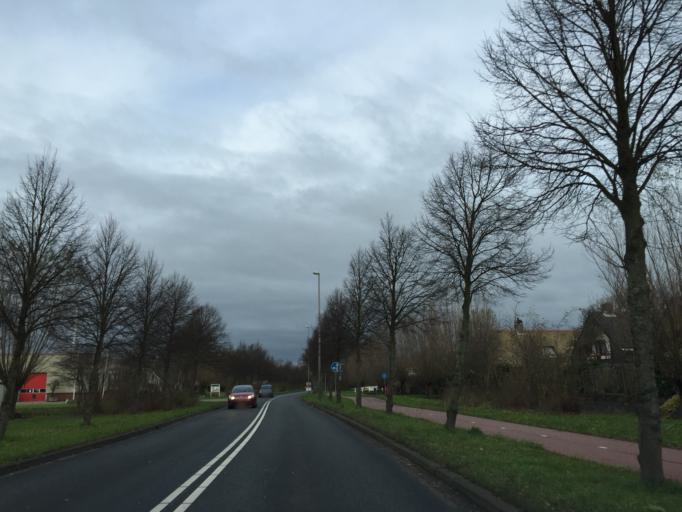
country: NL
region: South Holland
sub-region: Gemeente Pijnacker-Nootdorp
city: Pijnacker
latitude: 52.0211
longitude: 4.4267
